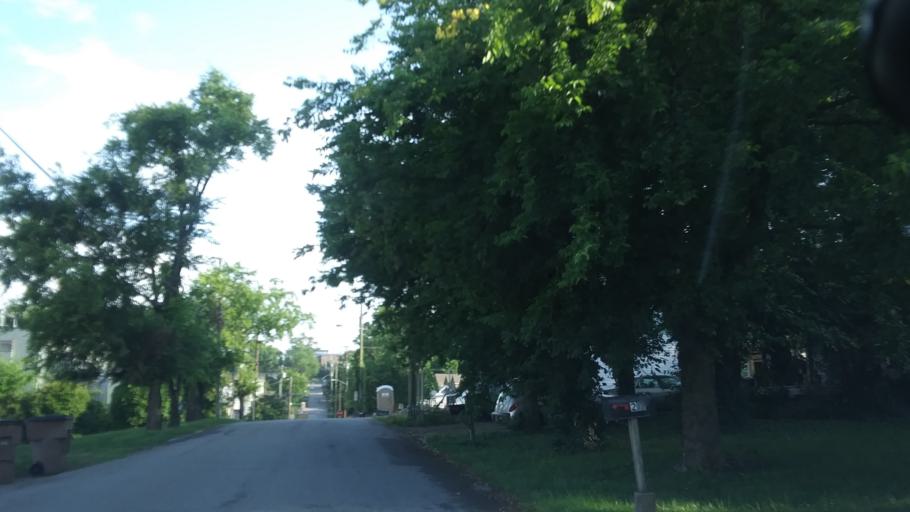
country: US
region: Tennessee
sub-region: Davidson County
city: Belle Meade
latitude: 36.1463
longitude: -86.8596
